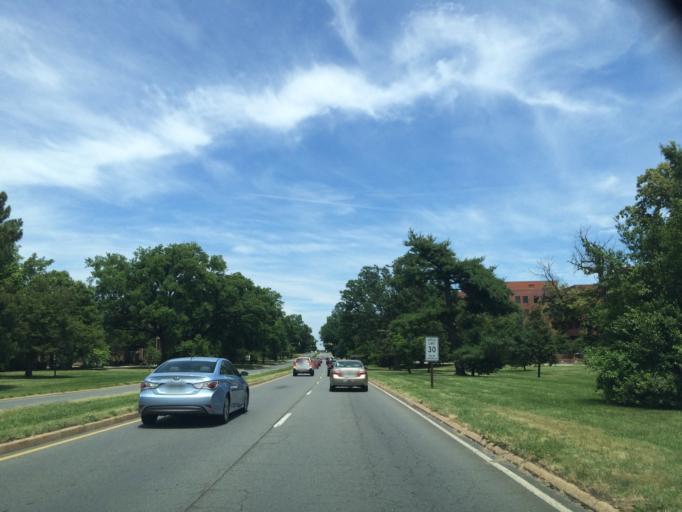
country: US
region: Virginia
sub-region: City of Alexandria
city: Alexandria
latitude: 38.8164
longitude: -77.0445
